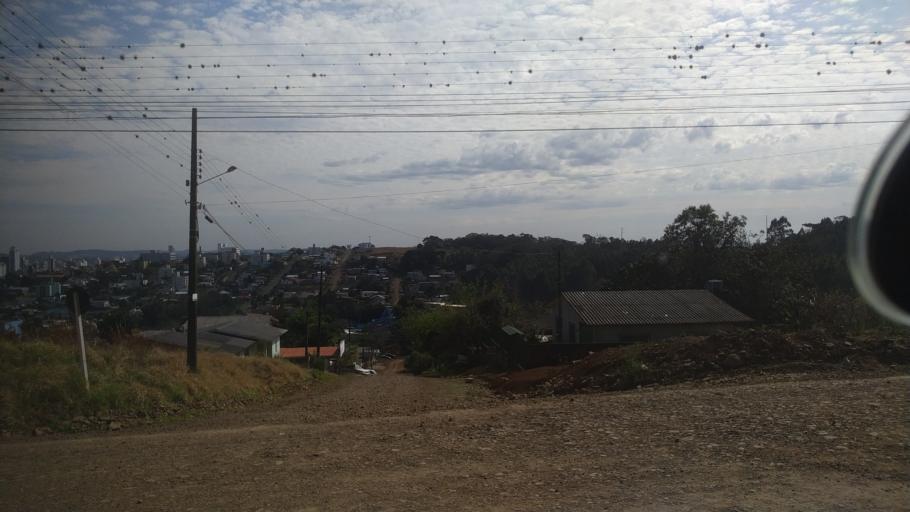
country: BR
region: Santa Catarina
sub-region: Chapeco
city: Chapeco
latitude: -27.1189
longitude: -52.5916
